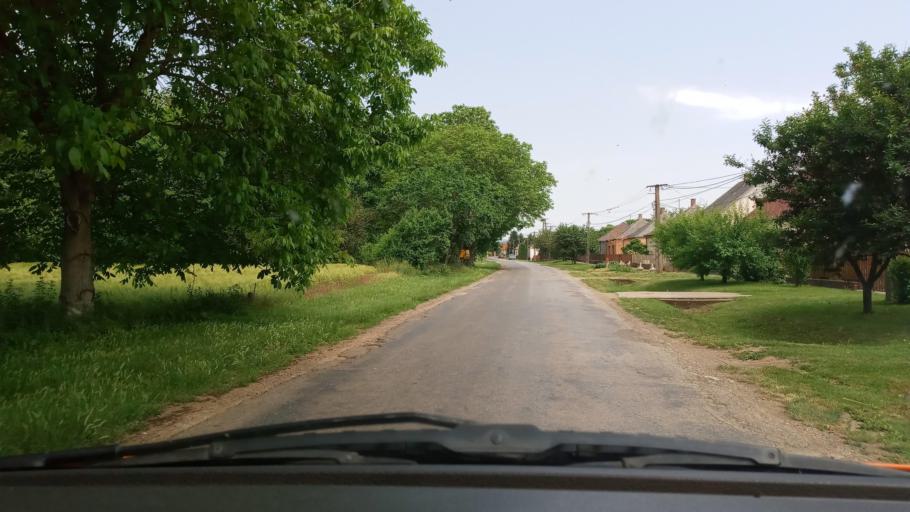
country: HU
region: Baranya
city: Szentlorinc
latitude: 46.0037
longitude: 18.0381
